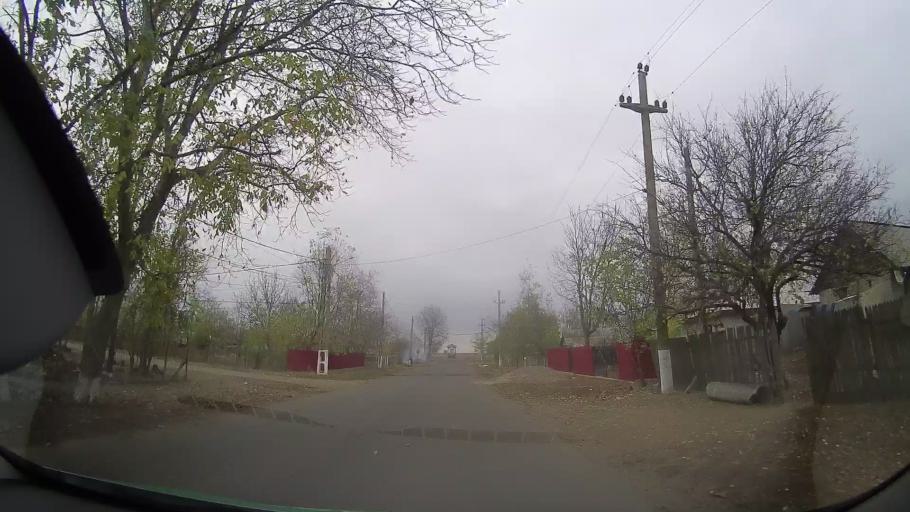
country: RO
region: Braila
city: Dudesti
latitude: 44.9418
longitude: 27.4247
